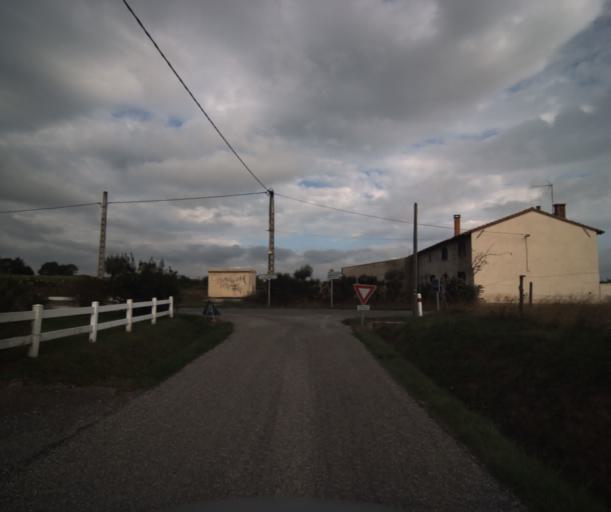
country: FR
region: Midi-Pyrenees
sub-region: Departement de la Haute-Garonne
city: Le Fauga
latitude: 43.4376
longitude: 1.2877
